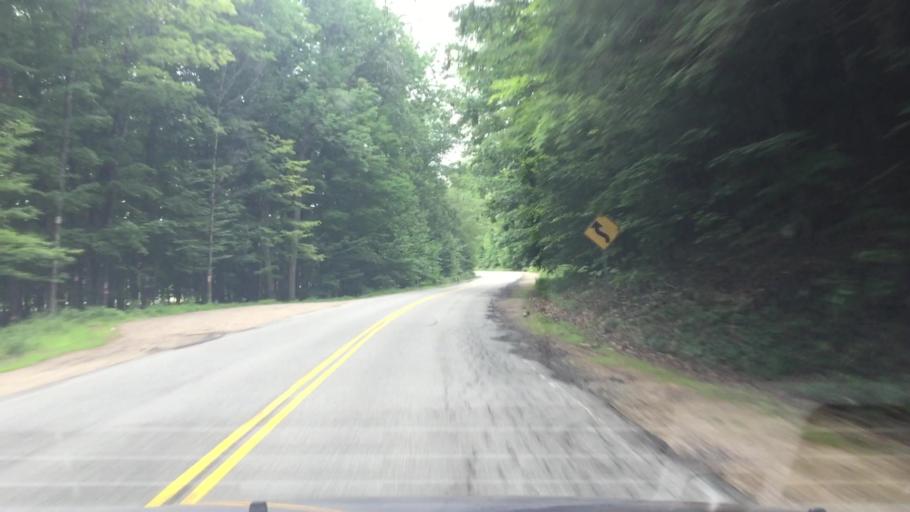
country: US
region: New Hampshire
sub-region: Carroll County
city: North Conway
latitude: 44.0978
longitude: -71.1720
